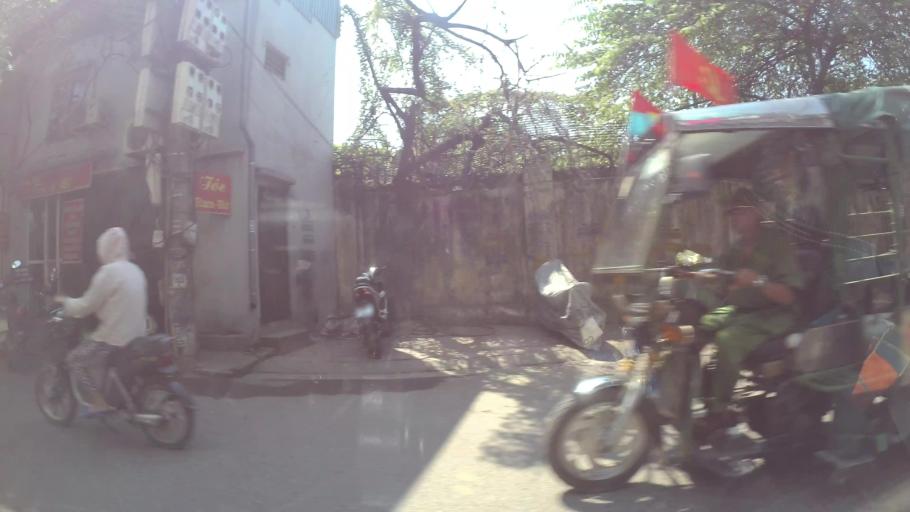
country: VN
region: Ha Noi
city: Hoan Kiem
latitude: 21.0510
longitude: 105.8780
